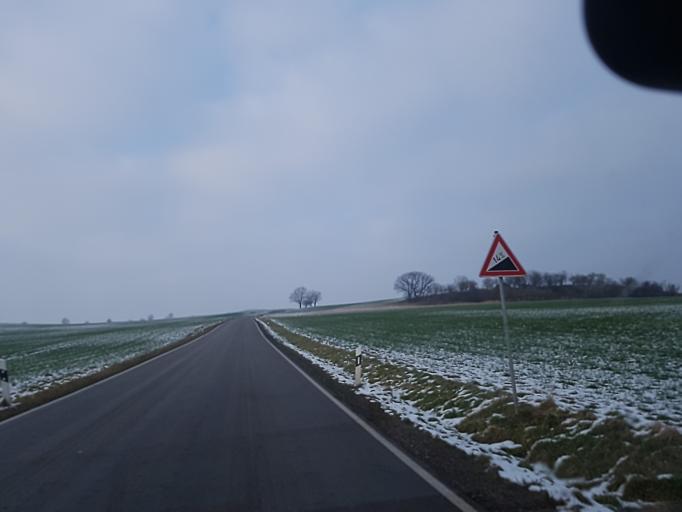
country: DE
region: Saxony
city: Cavertitz
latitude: 51.3494
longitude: 13.1392
